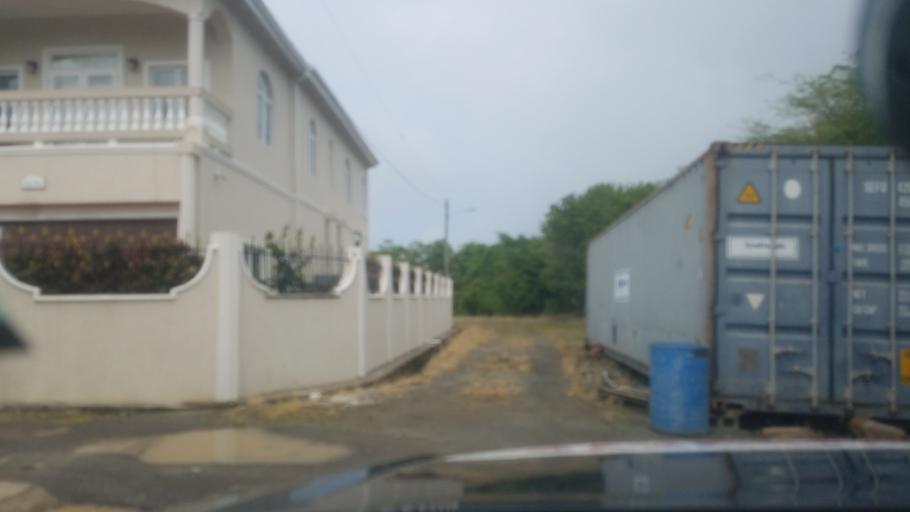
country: LC
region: Laborie Quarter
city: Laborie
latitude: 13.7479
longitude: -60.9740
